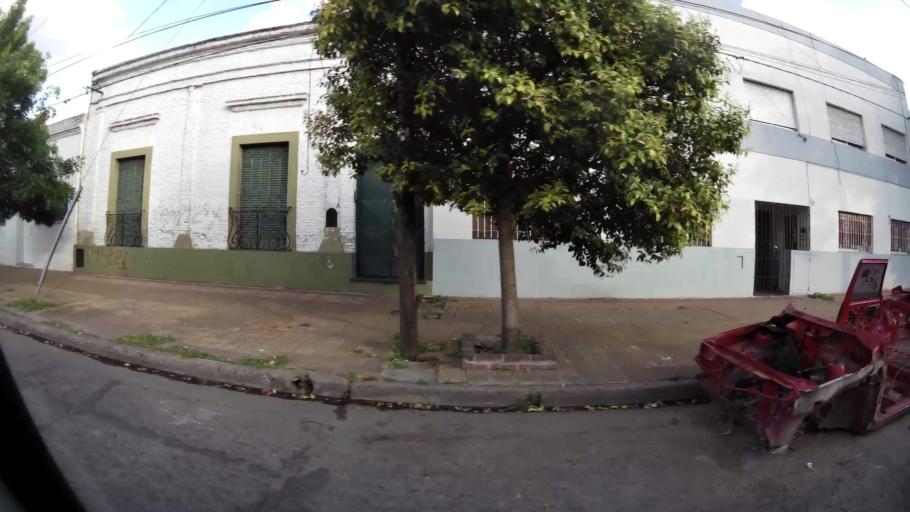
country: AR
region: Buenos Aires
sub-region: Partido de La Plata
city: La Plata
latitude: -34.8967
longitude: -57.9523
